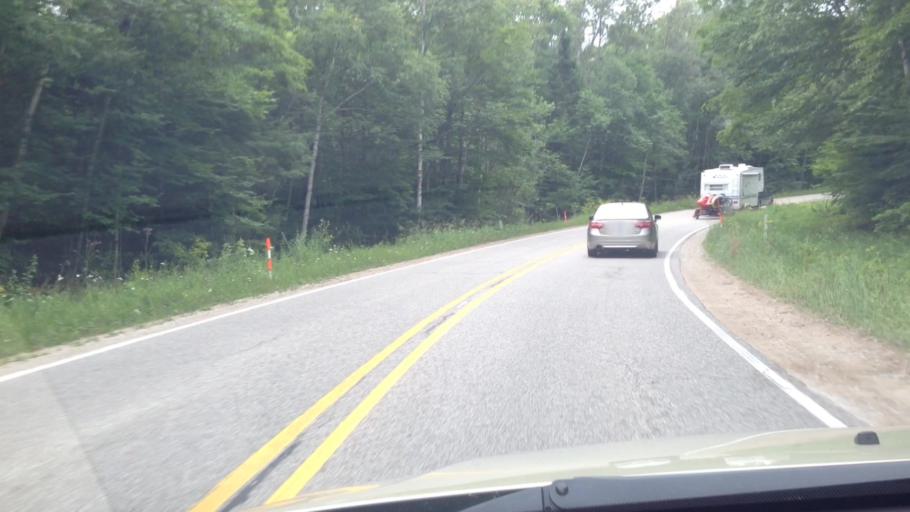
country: US
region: Michigan
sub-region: Mackinac County
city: Saint Ignace
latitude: 46.0487
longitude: -85.1053
